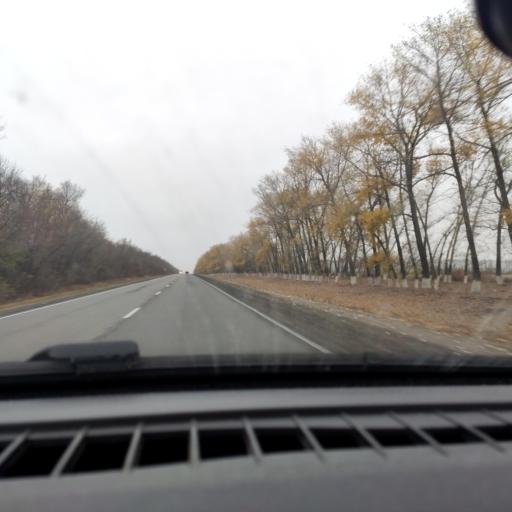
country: RU
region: Voronezj
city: Ostrogozhsk
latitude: 50.8854
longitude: 39.0705
